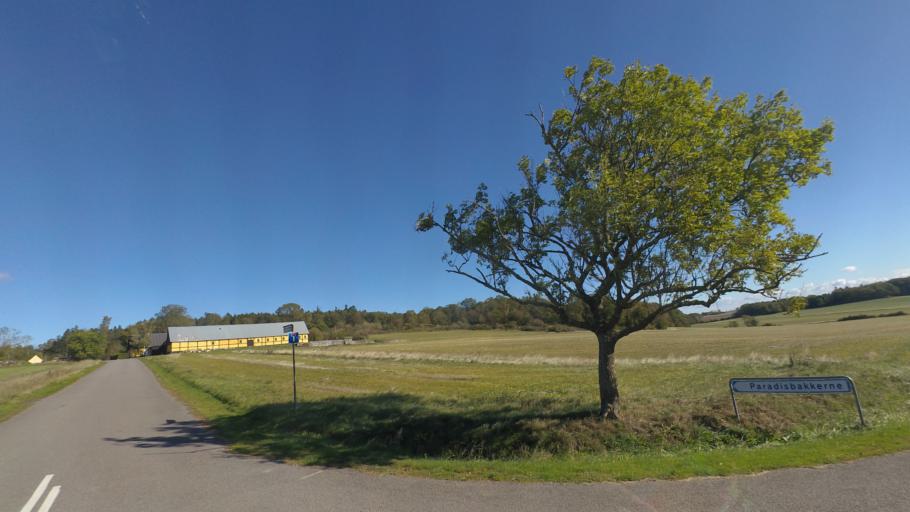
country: DK
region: Capital Region
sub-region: Bornholm Kommune
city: Nexo
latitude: 55.0789
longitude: 15.1008
